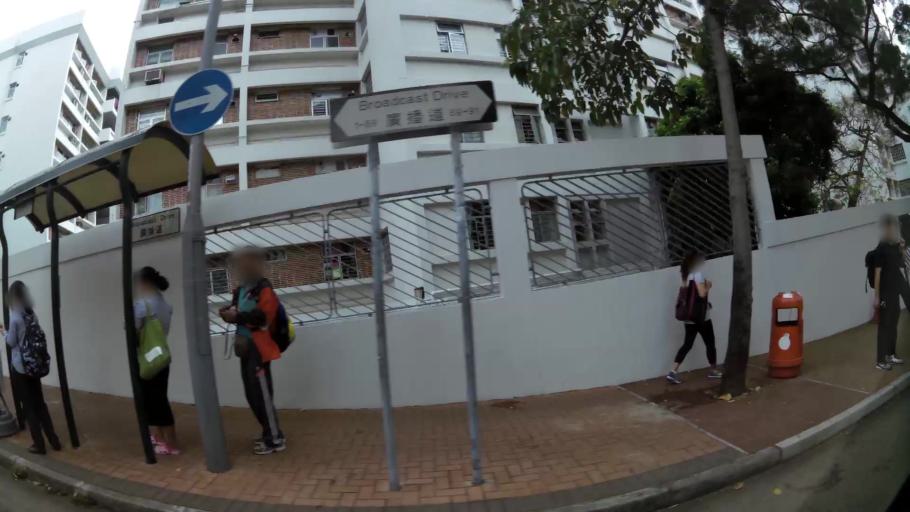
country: HK
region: Wong Tai Sin
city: Wong Tai Sin
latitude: 22.3410
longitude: 114.1827
